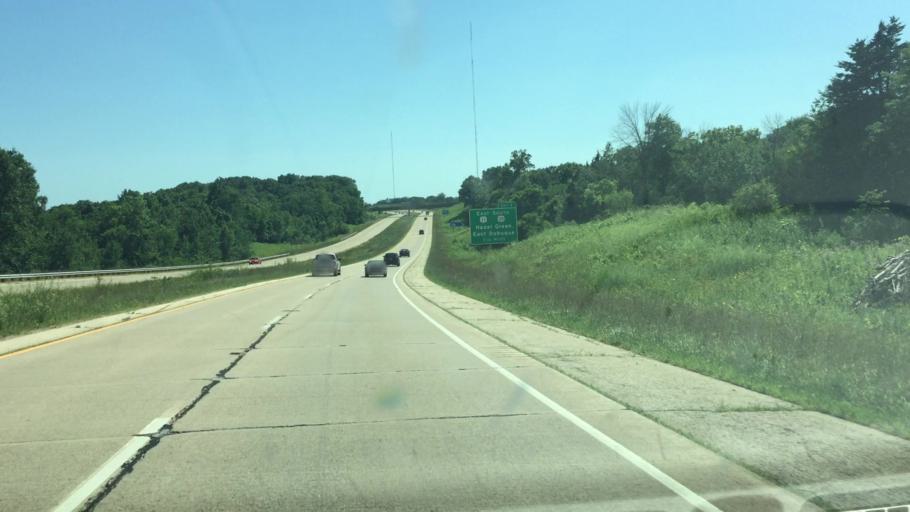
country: US
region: Illinois
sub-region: Jo Daviess County
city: East Dubuque
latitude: 42.5411
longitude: -90.6081
